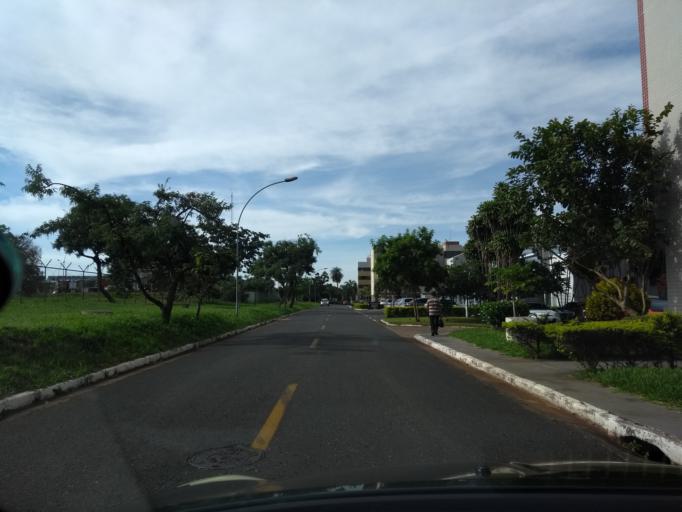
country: BR
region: Federal District
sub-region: Brasilia
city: Brasilia
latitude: -15.7843
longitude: -47.9264
